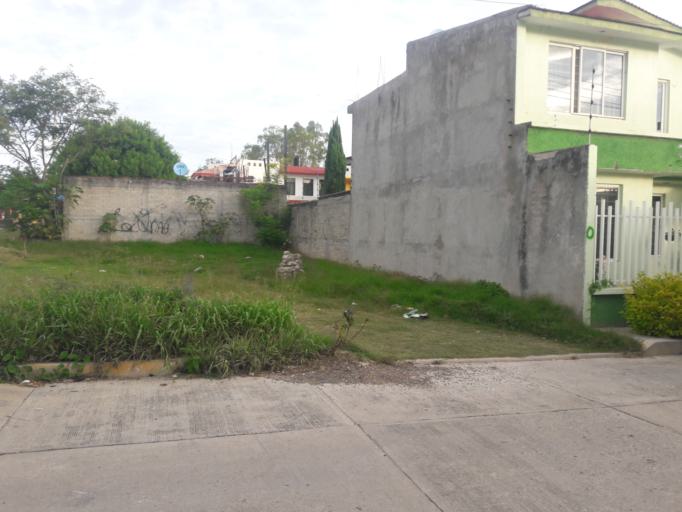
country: MX
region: Oaxaca
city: Ciudad de Huajuapam de Leon
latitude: 17.8022
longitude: -97.7855
